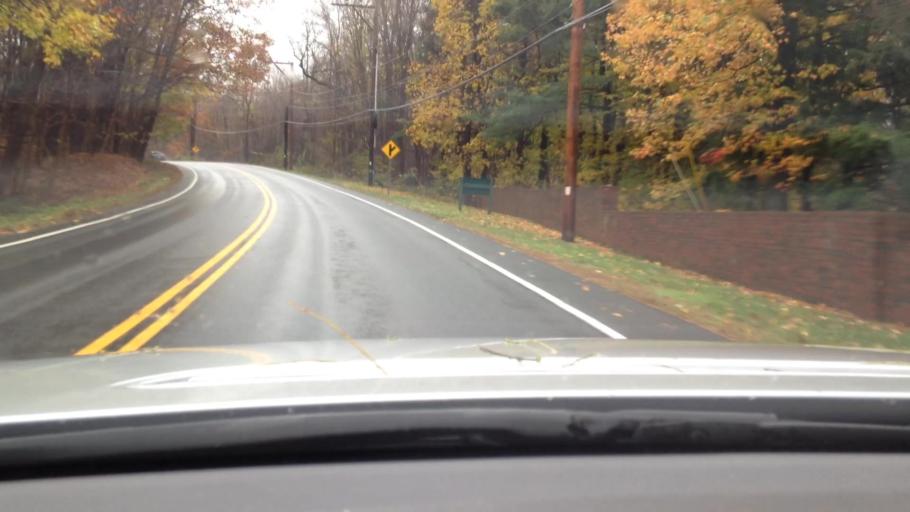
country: US
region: New York
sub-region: Putnam County
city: Cold Spring
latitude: 41.4127
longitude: -73.9378
